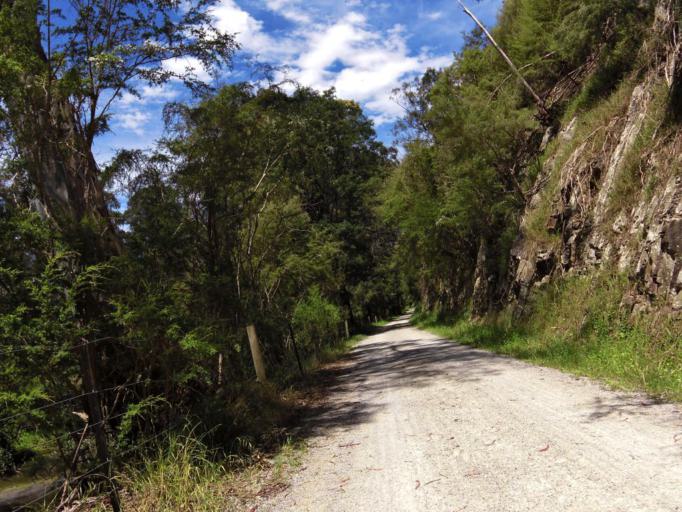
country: AU
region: Victoria
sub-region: Yarra Ranges
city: Woori Yallock
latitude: -37.7661
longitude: 145.5515
